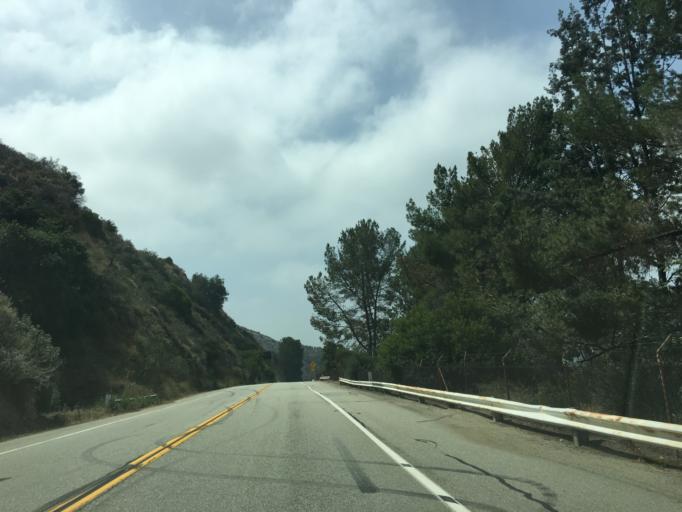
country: US
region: California
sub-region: Los Angeles County
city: Glendora
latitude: 34.1586
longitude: -117.8379
